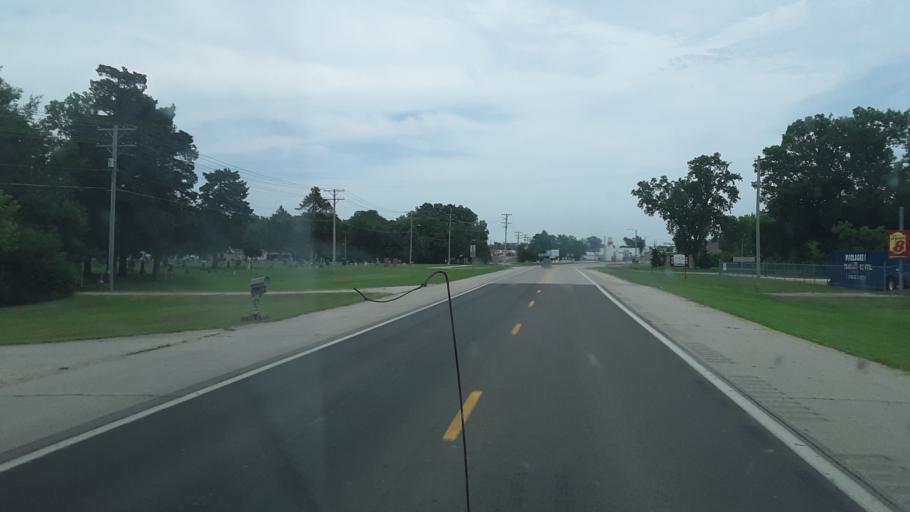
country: US
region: Kansas
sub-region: Allen County
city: Iola
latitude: 37.9220
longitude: -95.4156
